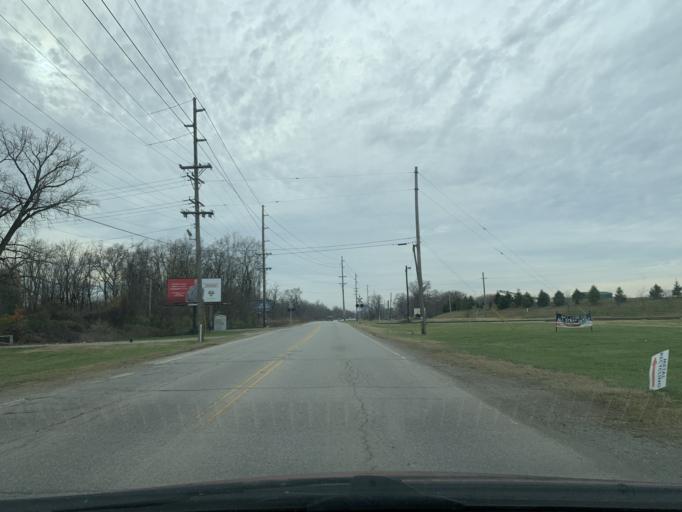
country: US
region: Indiana
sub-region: Clark County
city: Jeffersonville
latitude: 38.2690
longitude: -85.7143
